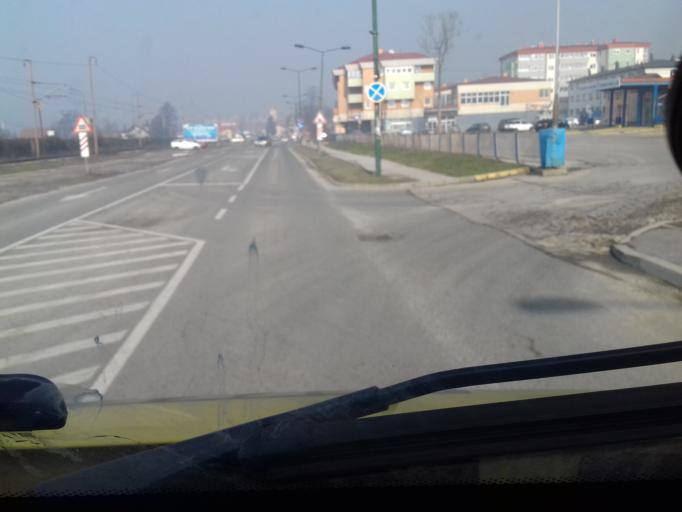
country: BA
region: Federation of Bosnia and Herzegovina
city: Ilijas
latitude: 43.9588
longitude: 18.2645
